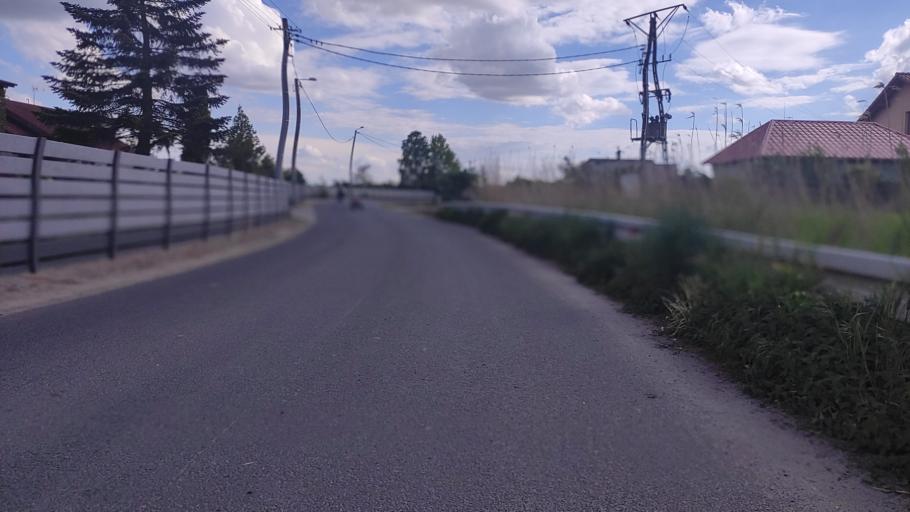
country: PL
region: Greater Poland Voivodeship
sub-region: Powiat poznanski
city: Kostrzyn
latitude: 52.4124
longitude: 17.1710
